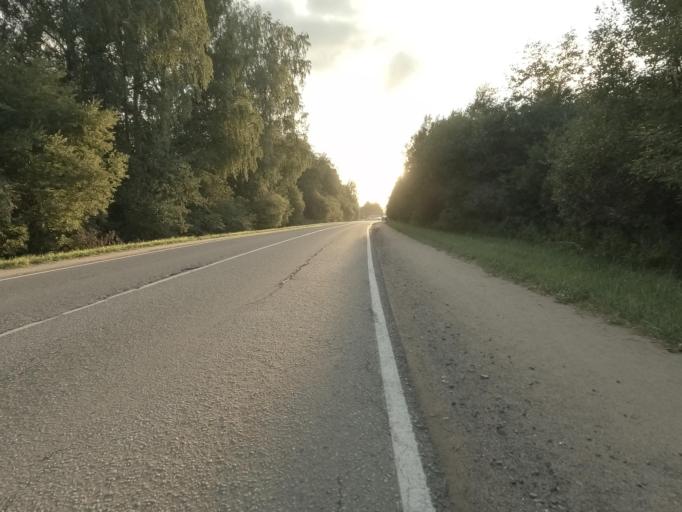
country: RU
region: Leningrad
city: Mga
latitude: 59.7625
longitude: 30.9914
